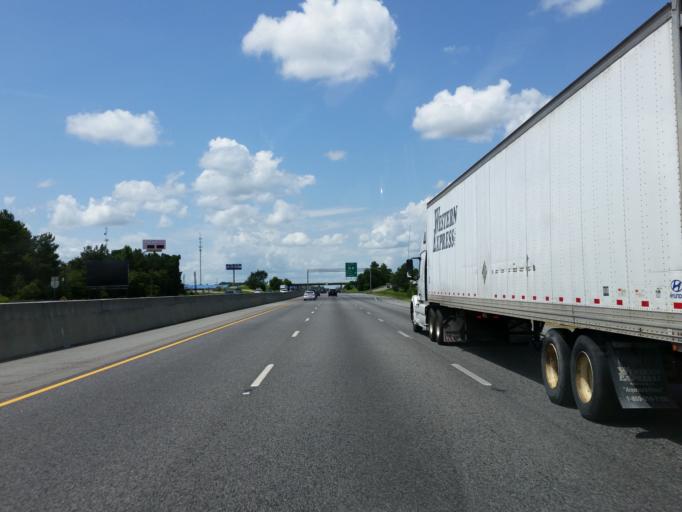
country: US
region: Georgia
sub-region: Lowndes County
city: Hahira
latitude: 30.9871
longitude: -83.3864
